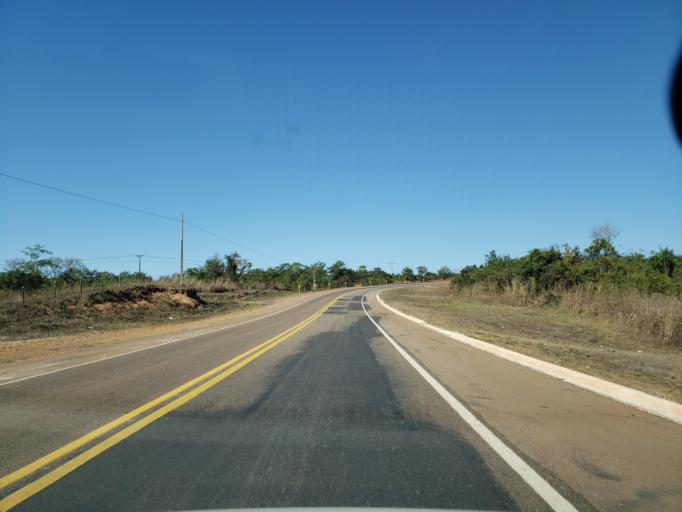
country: BR
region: Mato Grosso
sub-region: Poxoreo
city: Poxoreo
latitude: -15.7773
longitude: -54.3675
